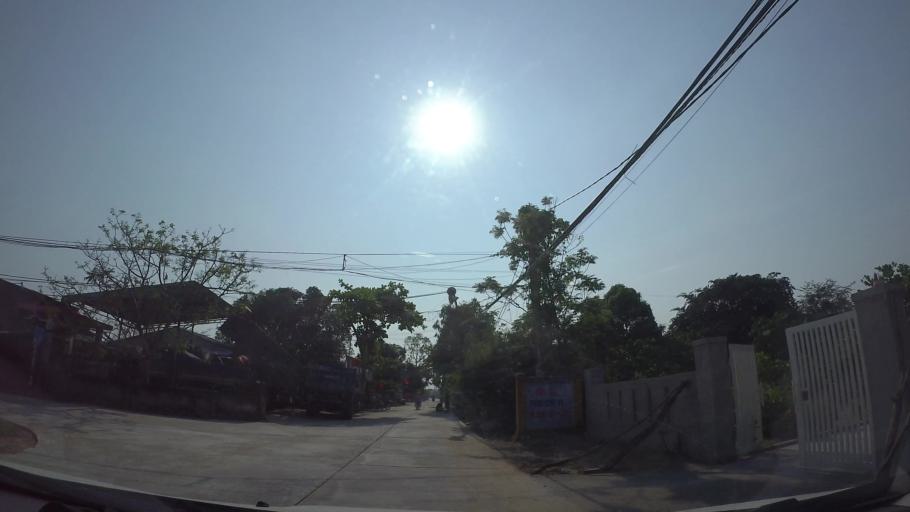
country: VN
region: Da Nang
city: Ngu Hanh Son
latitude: 15.9579
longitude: 108.2603
